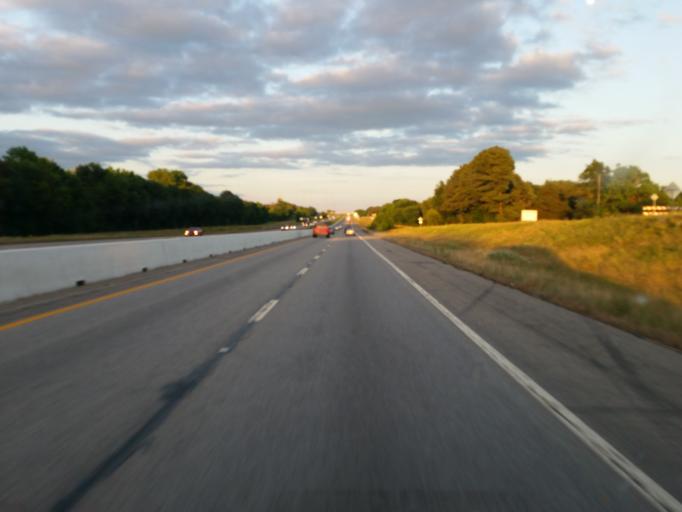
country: US
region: Texas
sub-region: Van Zandt County
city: Van
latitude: 32.5100
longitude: -95.6630
